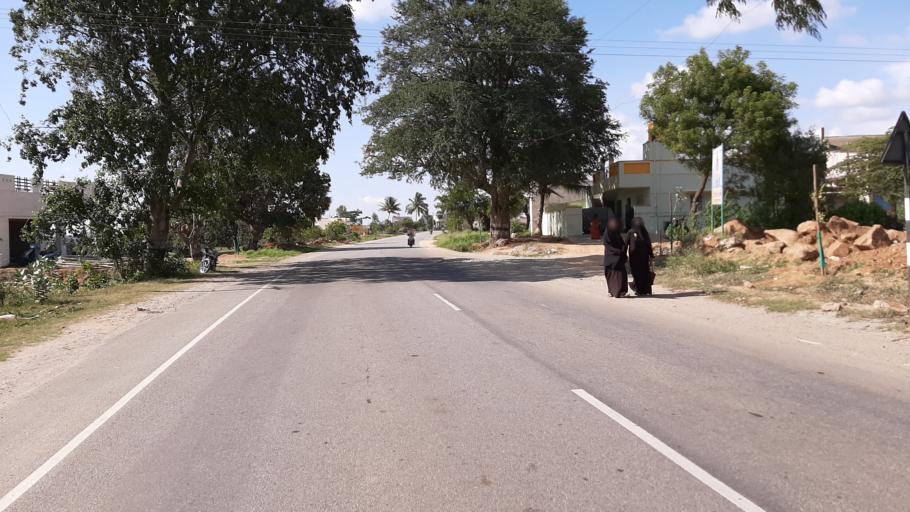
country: IN
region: Tamil Nadu
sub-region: Krishnagiri
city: Denkanikota
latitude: 12.5523
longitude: 77.7858
